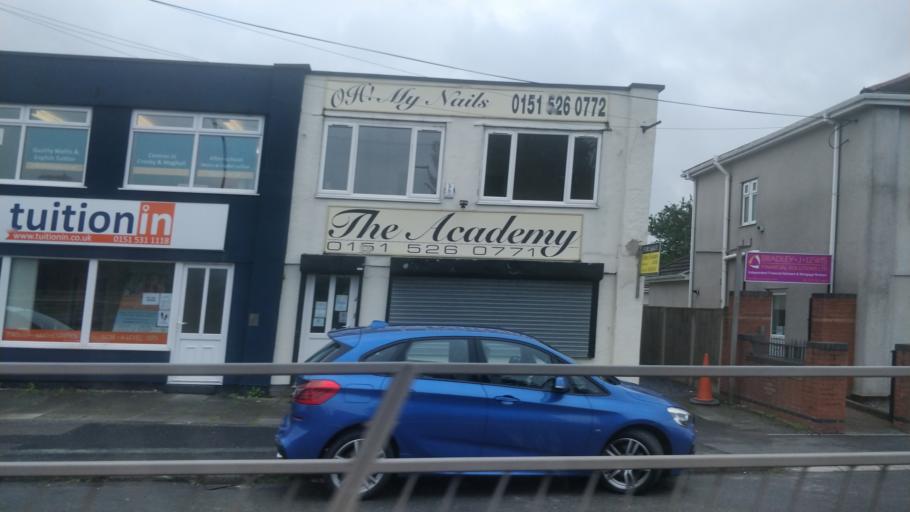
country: GB
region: England
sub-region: Sefton
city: Maghull
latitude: 53.4988
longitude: -2.9474
